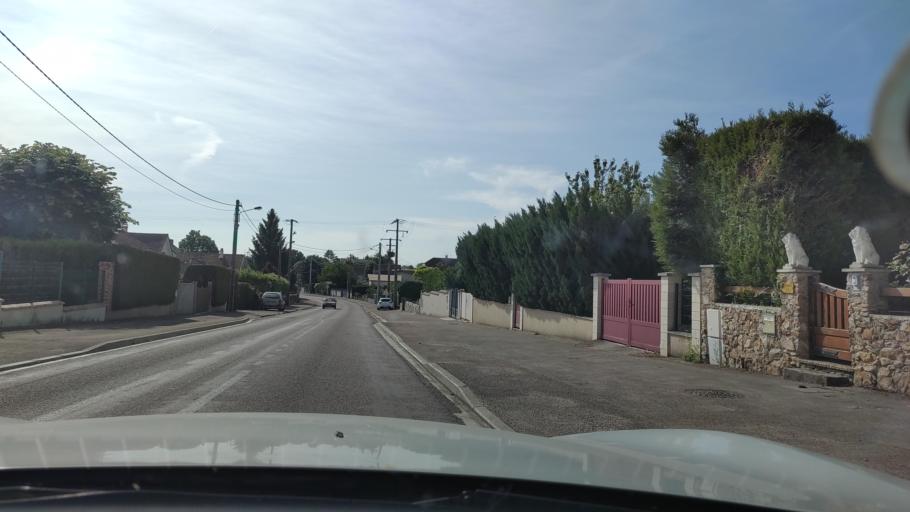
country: FR
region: Champagne-Ardenne
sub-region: Departement de l'Aube
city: Nogent-sur-Seine
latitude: 48.4772
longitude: 3.5513
